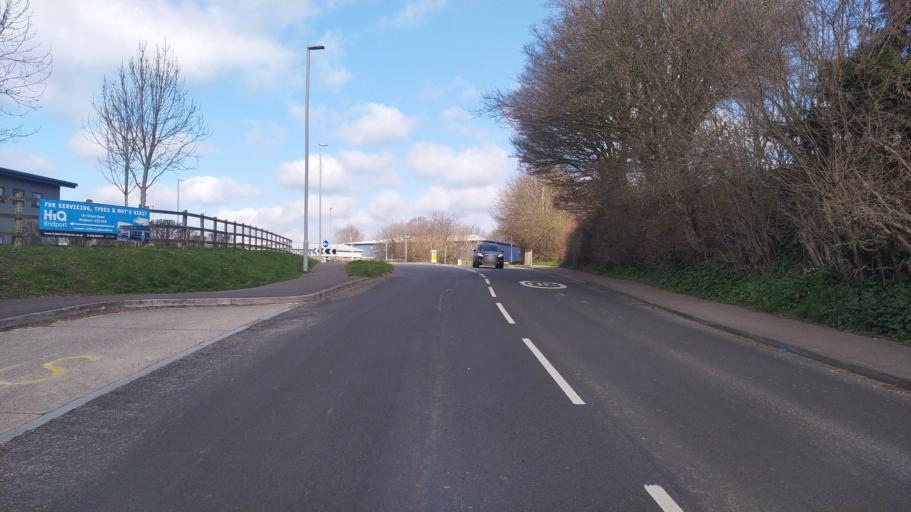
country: GB
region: England
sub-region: Dorset
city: Bridport
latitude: 50.7471
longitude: -2.7429
